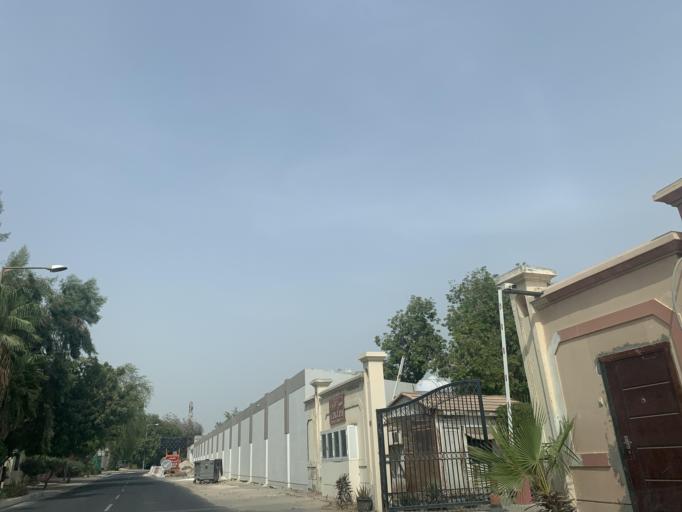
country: BH
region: Manama
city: Jidd Hafs
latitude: 26.2070
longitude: 50.4761
